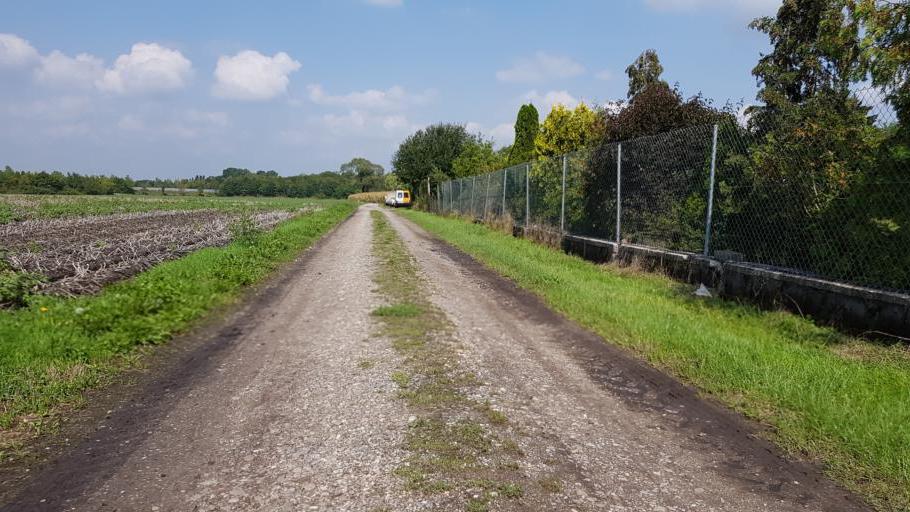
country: DE
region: Bavaria
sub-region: Upper Bavaria
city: Karlsfeld
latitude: 48.2093
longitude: 11.5011
